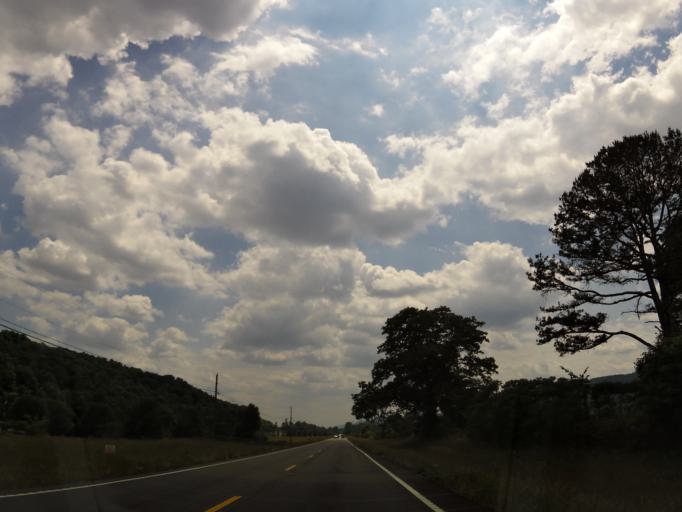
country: US
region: Tennessee
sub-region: Sequatchie County
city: Dunlap
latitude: 35.4813
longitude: -85.3102
